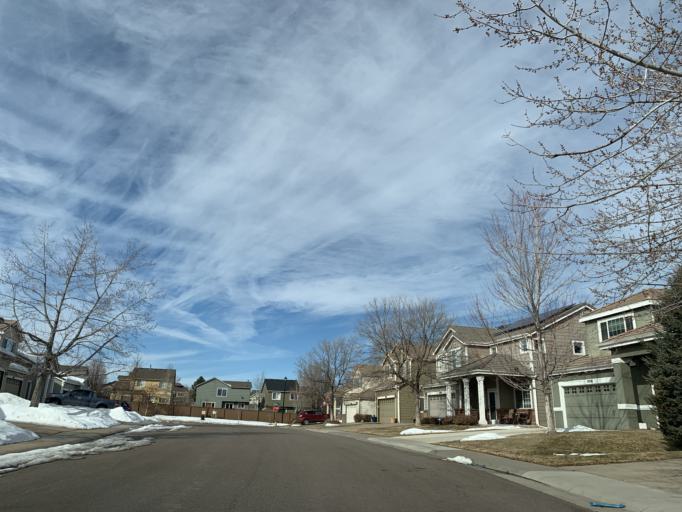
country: US
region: Colorado
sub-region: Douglas County
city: Carriage Club
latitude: 39.5287
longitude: -104.9323
